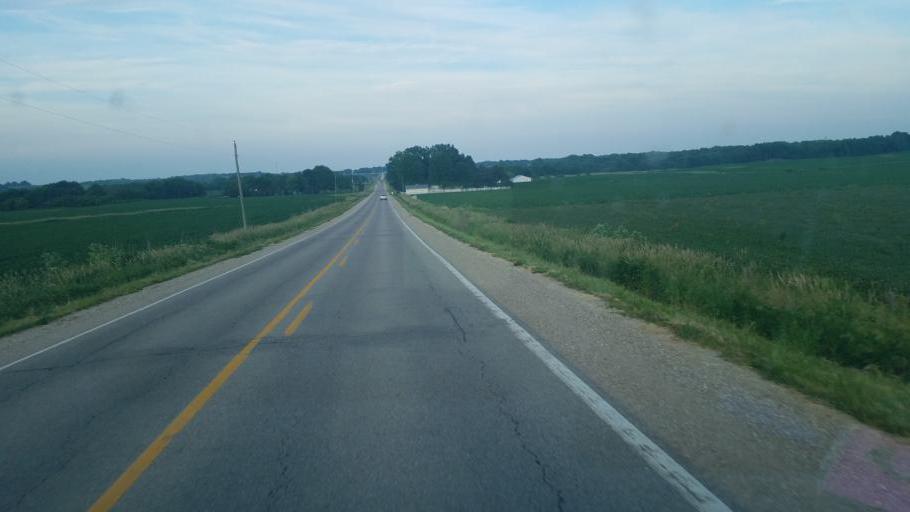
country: US
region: Iowa
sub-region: Benton County
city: Belle Plaine
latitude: 41.9061
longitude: -92.3163
